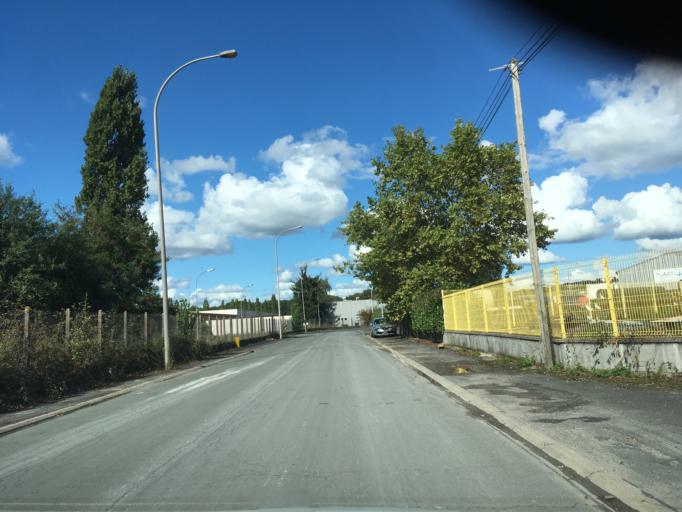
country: FR
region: Limousin
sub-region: Departement de la Correze
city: Saint-Pantaleon-de-Larche
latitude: 45.1511
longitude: 1.4781
